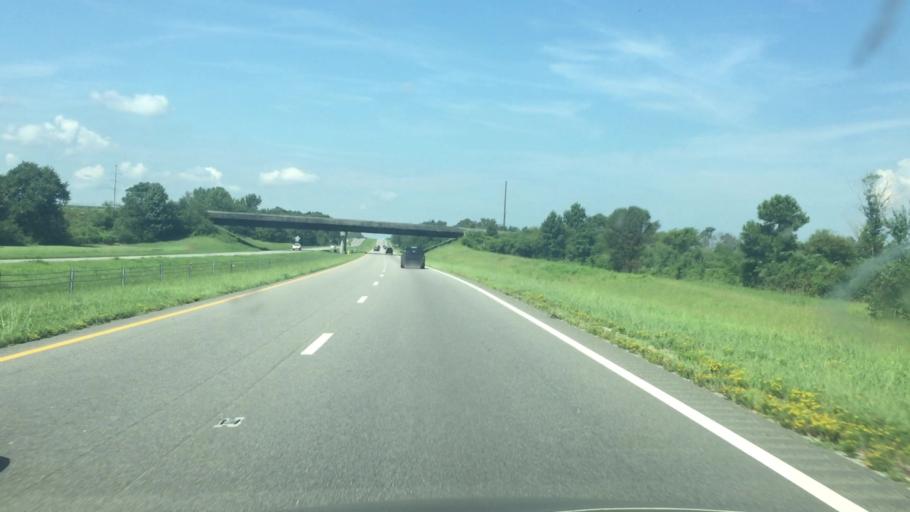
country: US
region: North Carolina
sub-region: Robeson County
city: Maxton
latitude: 34.7626
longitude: -79.4020
